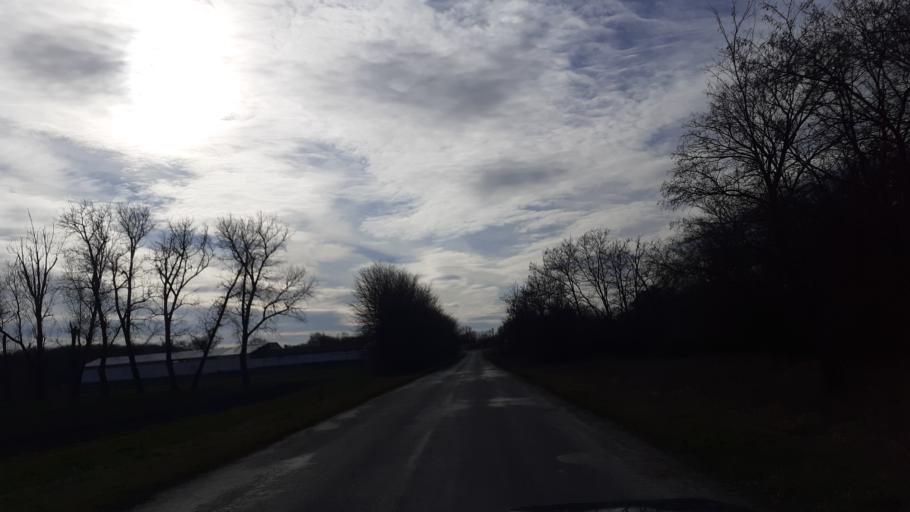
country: HU
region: Fejer
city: Kaloz
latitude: 46.9062
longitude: 18.5225
